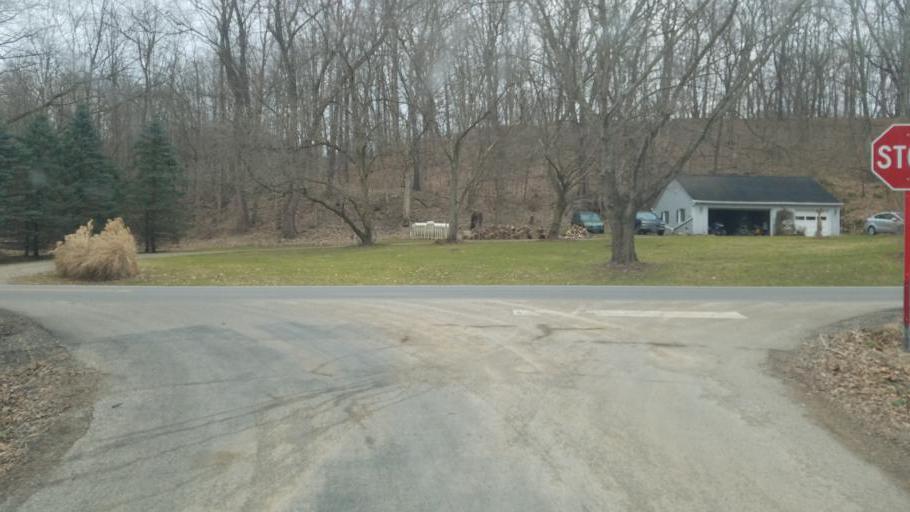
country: US
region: Ohio
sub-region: Richland County
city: Lincoln Heights
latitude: 40.7322
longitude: -82.3662
